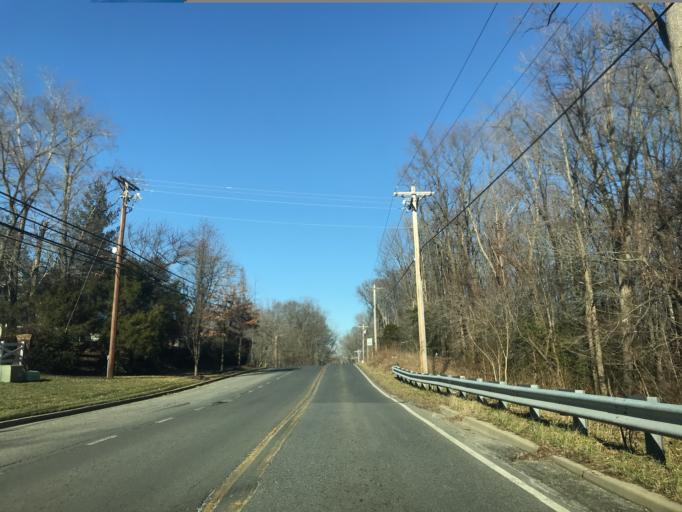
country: US
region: Maryland
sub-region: Prince George's County
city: Accokeek
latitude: 38.6767
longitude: -76.9883
